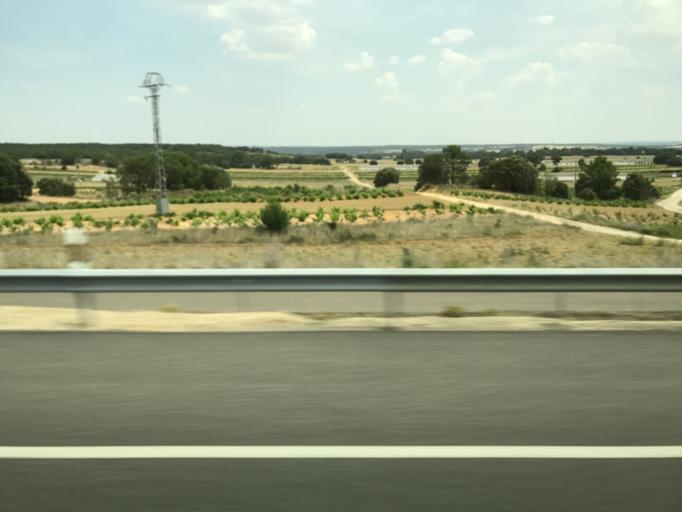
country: ES
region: Castille and Leon
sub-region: Provincia de Burgos
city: Aranda de Duero
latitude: 41.7153
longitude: -3.6882
